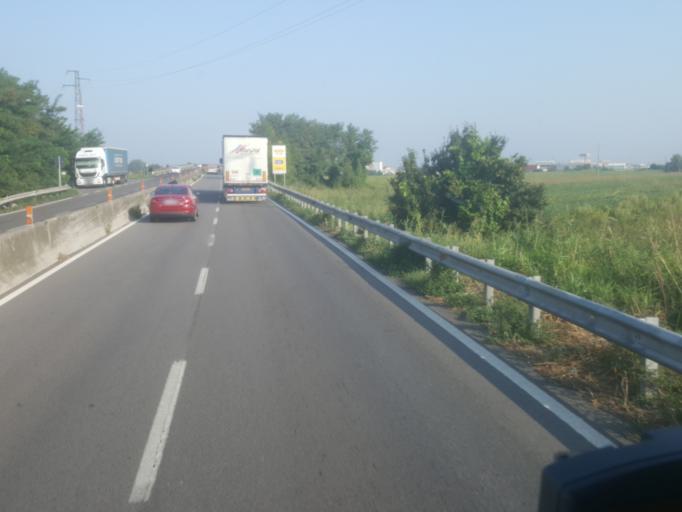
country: IT
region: Emilia-Romagna
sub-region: Provincia di Ravenna
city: Ravenna
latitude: 44.4178
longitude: 12.1676
